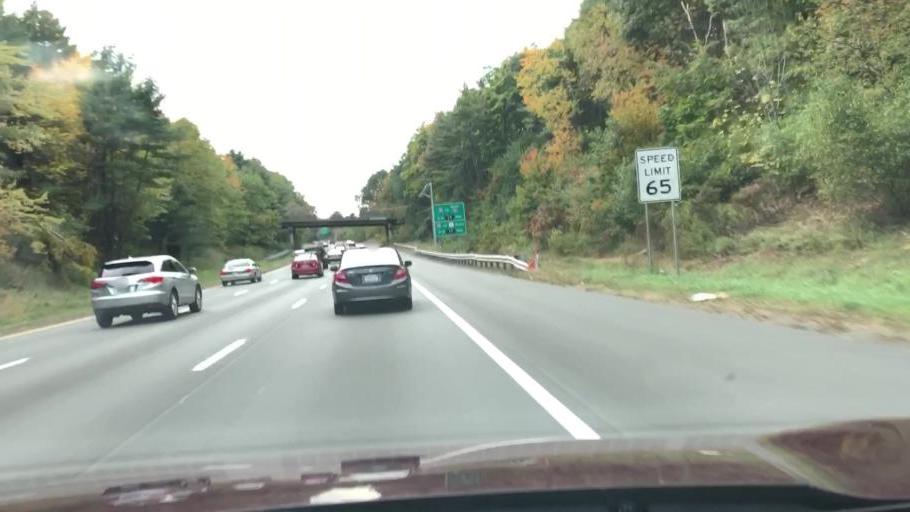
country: US
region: Massachusetts
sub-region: Essex County
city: Lawrence
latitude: 42.6729
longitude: -71.1793
